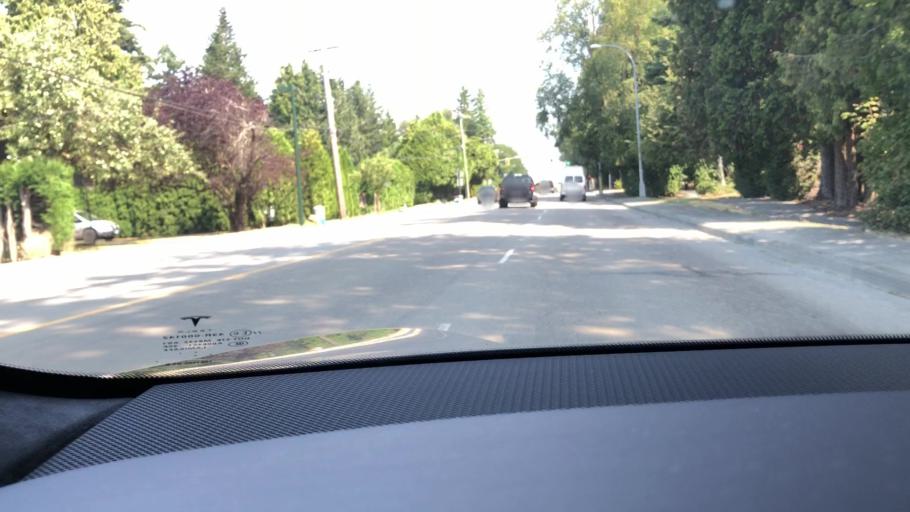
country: US
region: Washington
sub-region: Whatcom County
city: Point Roberts
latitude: 49.0165
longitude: -123.0686
